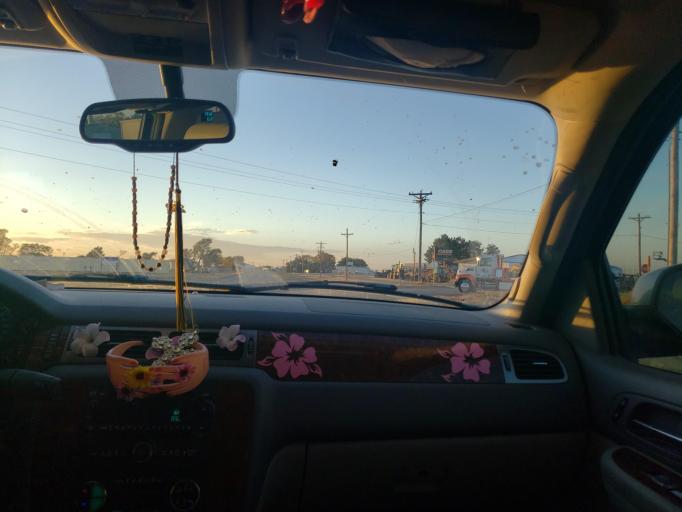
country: US
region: Kansas
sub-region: Finney County
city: Garden City
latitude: 37.9793
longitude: -100.8958
